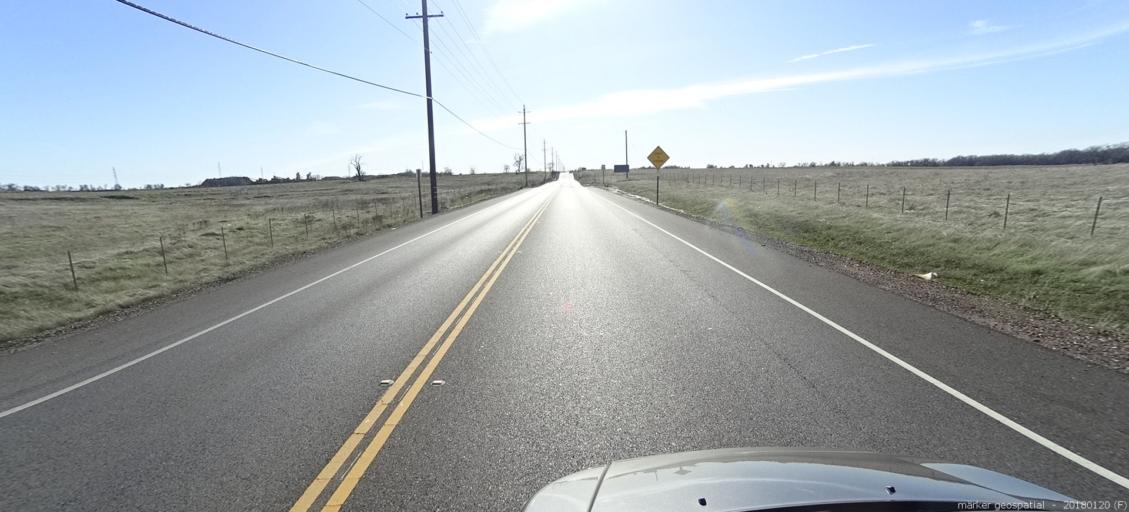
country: US
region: California
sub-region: Sacramento County
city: Gold River
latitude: 38.5927
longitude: -121.1791
